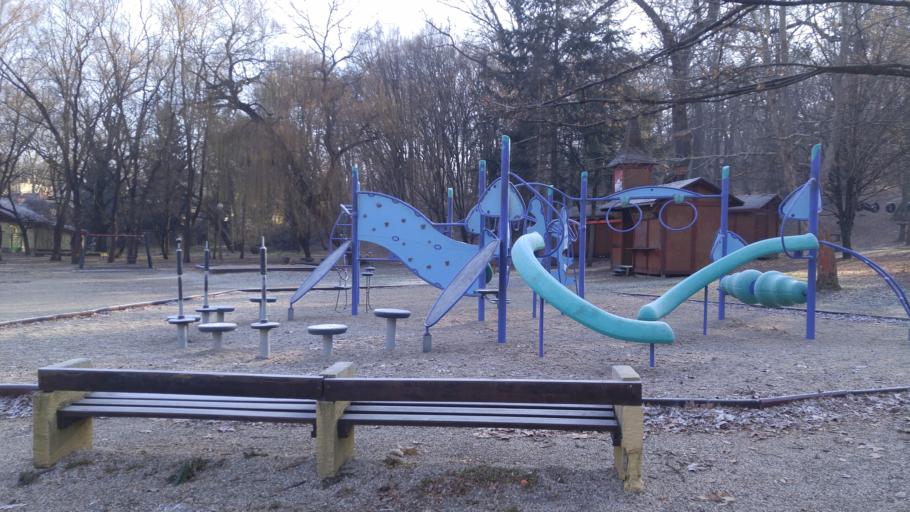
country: HU
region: Borsod-Abauj-Zemplen
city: Miskolc
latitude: 48.0601
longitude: 20.7481
